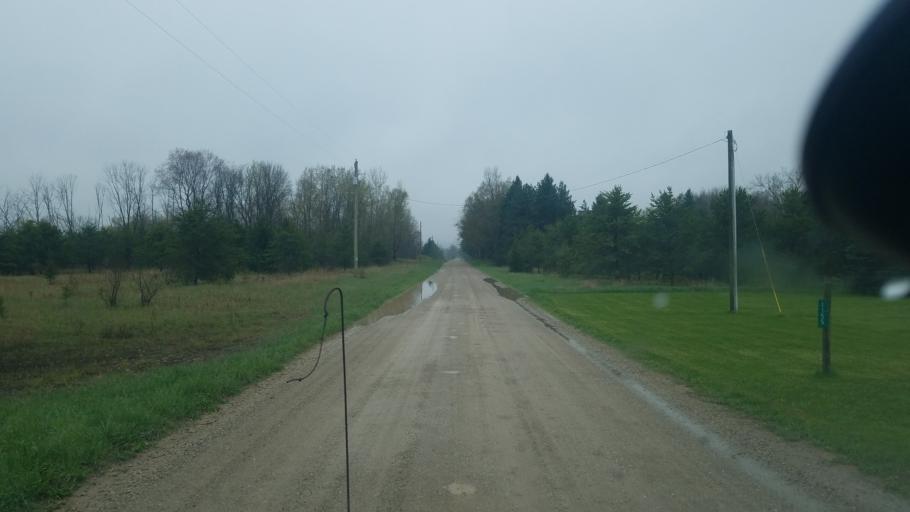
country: US
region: Michigan
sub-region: Montcalm County
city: Lakeview
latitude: 43.4857
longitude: -85.3333
